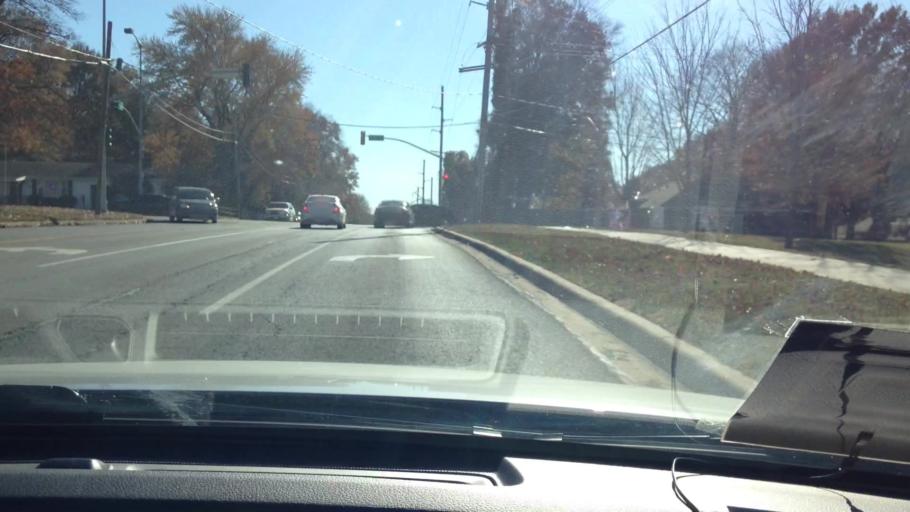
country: US
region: Missouri
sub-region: Jackson County
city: Raytown
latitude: 39.0375
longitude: -94.4481
